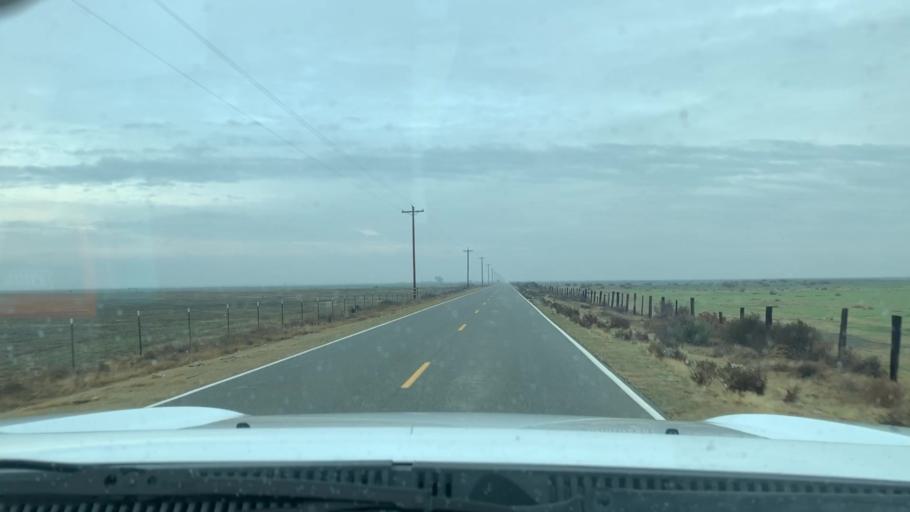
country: US
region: California
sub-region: Kern County
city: Lost Hills
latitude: 35.6865
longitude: -119.5798
